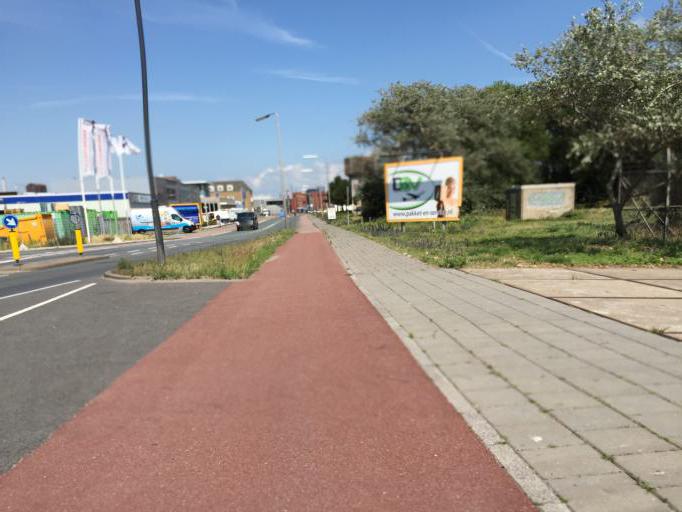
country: NL
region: North Holland
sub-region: Gemeente Velsen
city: Velsen-Zuid
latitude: 52.4551
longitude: 4.5924
